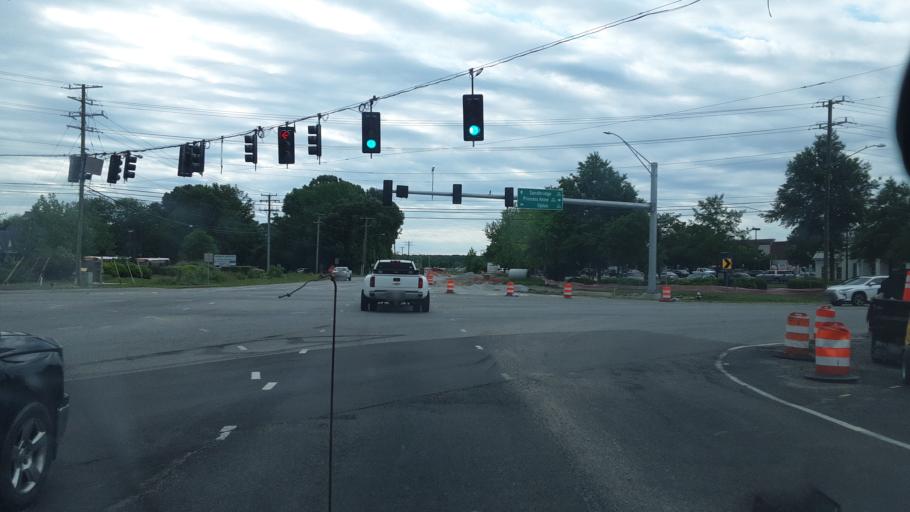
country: US
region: Virginia
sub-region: City of Virginia Beach
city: Virginia Beach
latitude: 36.7522
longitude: -76.0102
